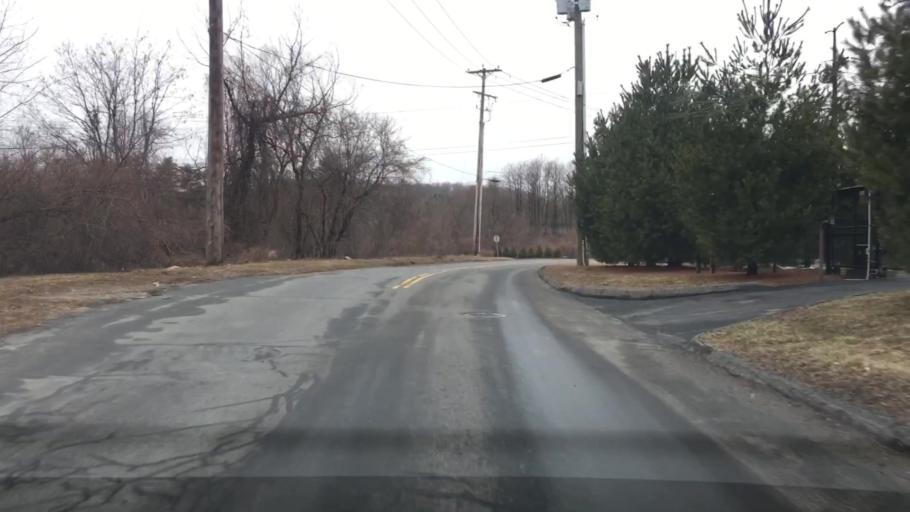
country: US
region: Connecticut
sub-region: Fairfield County
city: Bethel
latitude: 41.4378
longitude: -73.3978
